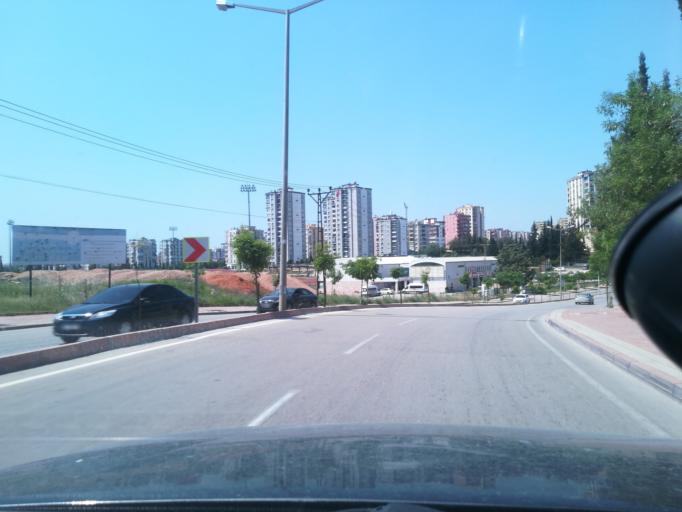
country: TR
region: Adana
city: Seyhan
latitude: 37.0335
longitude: 35.2689
